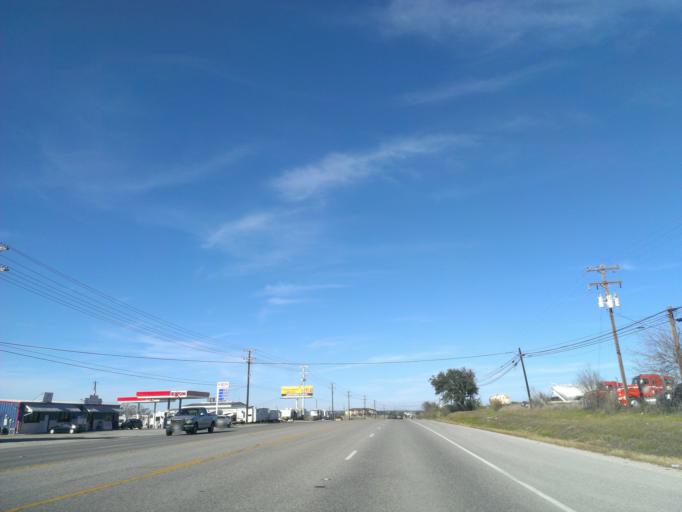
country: US
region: Texas
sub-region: Burnet County
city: Meadowlakes
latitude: 30.5458
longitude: -98.2768
